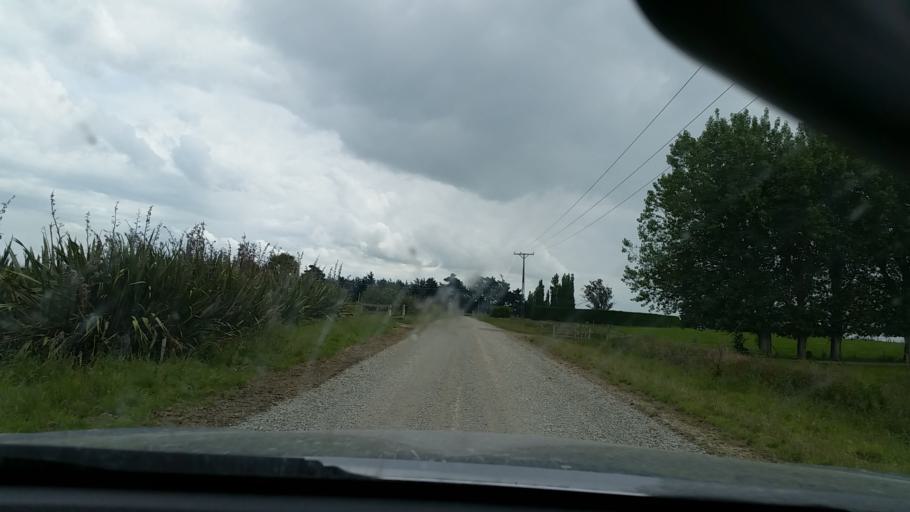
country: NZ
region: Southland
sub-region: Southland District
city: Winton
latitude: -46.0210
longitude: 168.2594
